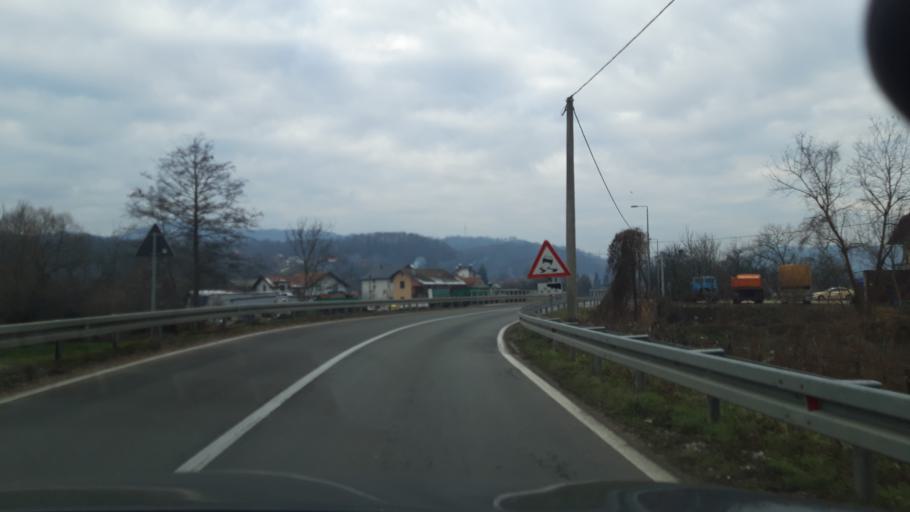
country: BA
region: Republika Srpska
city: Zvornik
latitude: 44.4110
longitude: 19.1475
